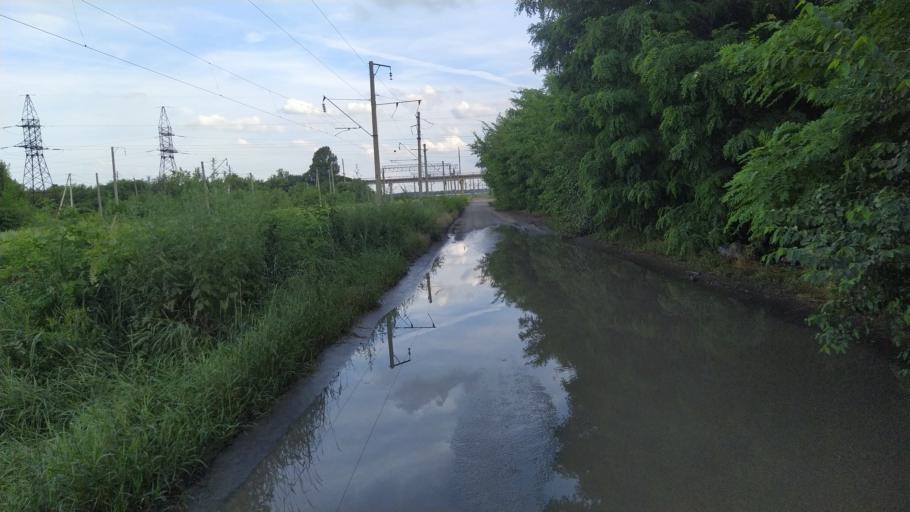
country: RU
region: Rostov
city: Bataysk
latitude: 47.1042
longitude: 39.7126
